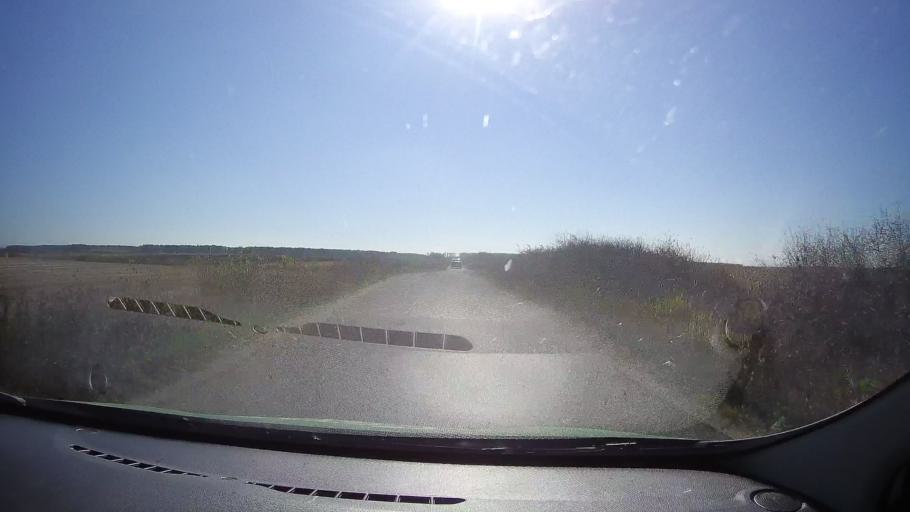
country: RO
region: Satu Mare
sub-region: Comuna Doba
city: Doba
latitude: 47.7283
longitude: 22.7242
